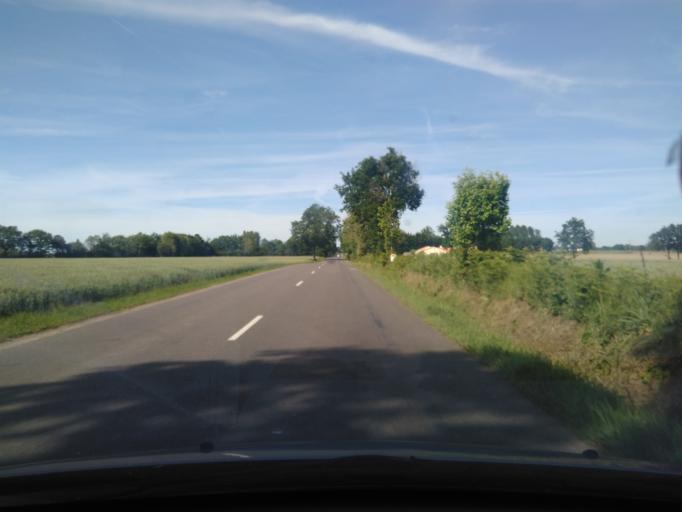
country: FR
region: Pays de la Loire
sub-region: Departement de la Vendee
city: Nieul-le-Dolent
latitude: 46.5284
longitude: -1.5486
